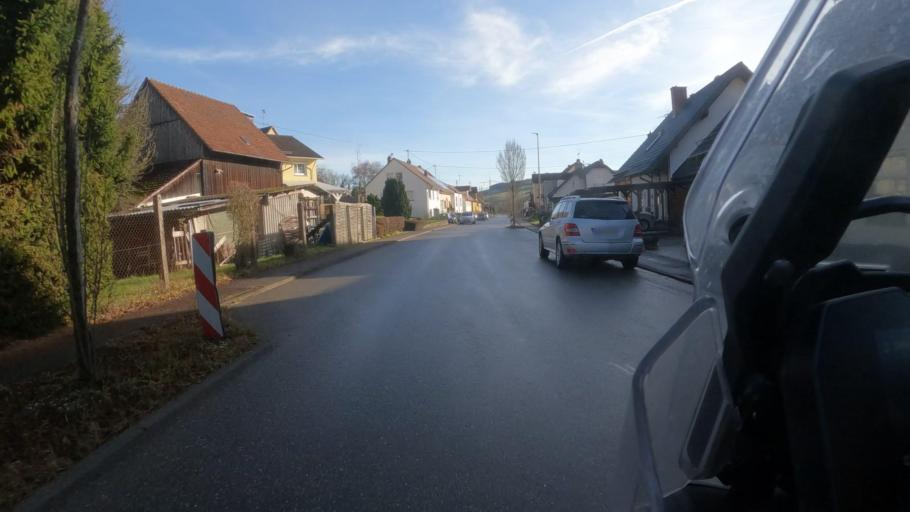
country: DE
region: Baden-Wuerttemberg
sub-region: Freiburg Region
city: Neuhausen
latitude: 47.8222
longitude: 8.7524
